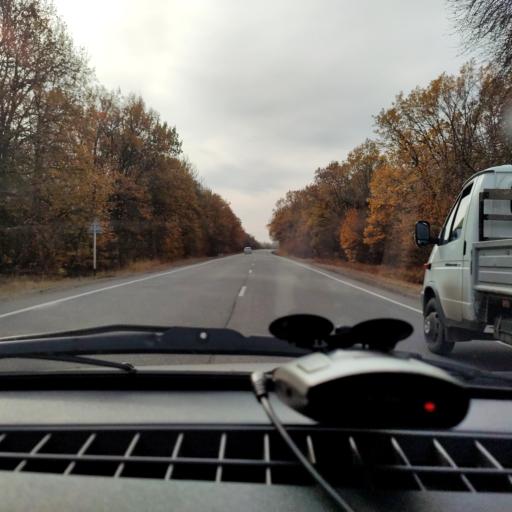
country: RU
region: Voronezj
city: Devitsa
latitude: 51.6147
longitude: 38.9827
